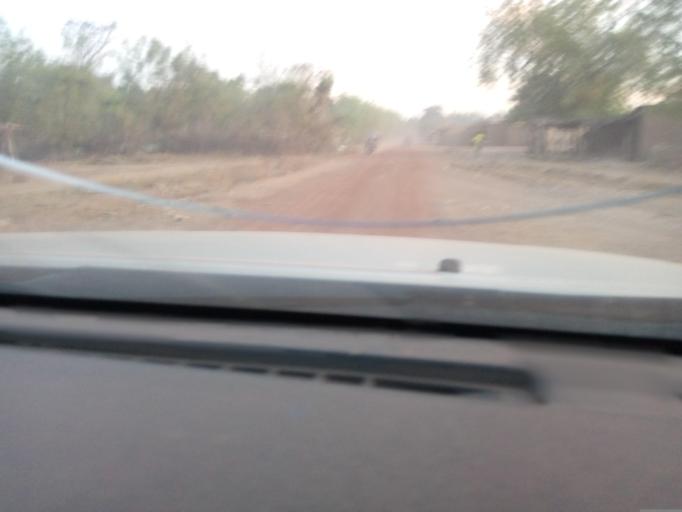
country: ML
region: Sikasso
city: Koutiala
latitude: 12.0991
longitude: -6.1414
